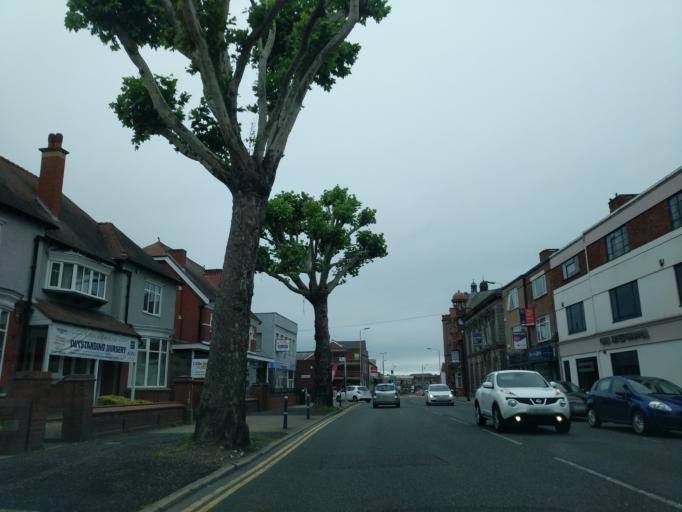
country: GB
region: England
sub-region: Dudley
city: Stourbridge
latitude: 52.4536
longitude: -2.1433
